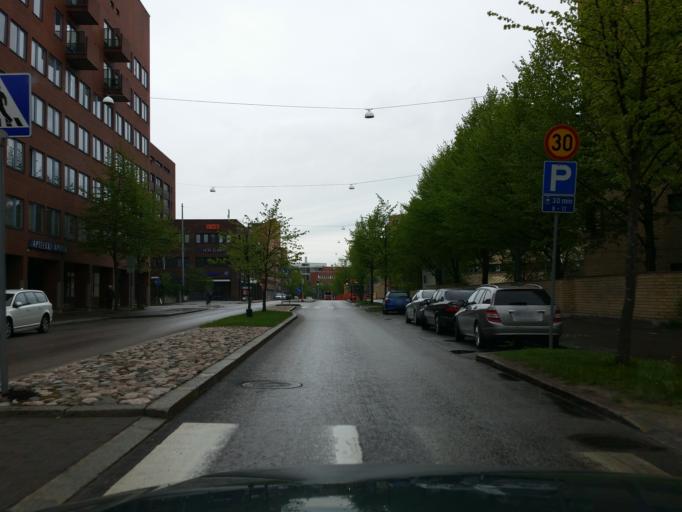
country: FI
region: Uusimaa
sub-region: Helsinki
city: Teekkarikylae
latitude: 60.2316
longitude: 24.8827
